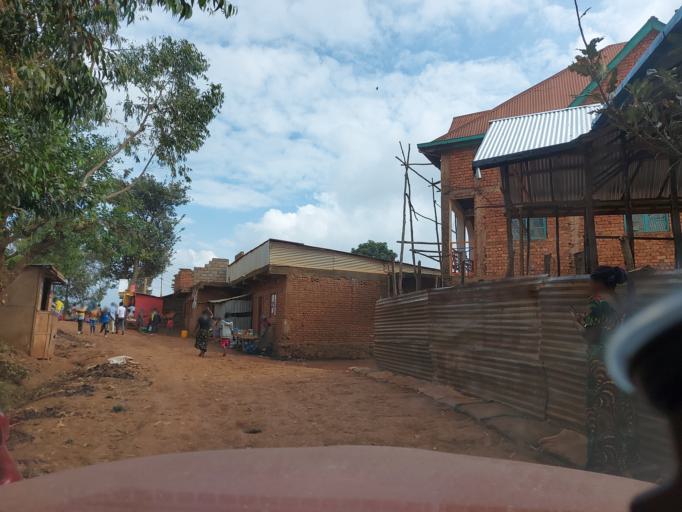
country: CD
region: South Kivu
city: Bukavu
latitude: -2.5136
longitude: 28.8383
